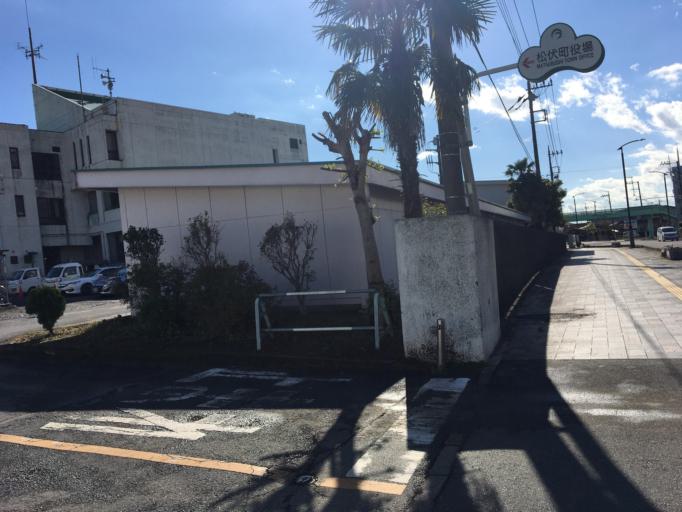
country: JP
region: Chiba
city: Noda
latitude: 35.9263
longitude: 139.8149
